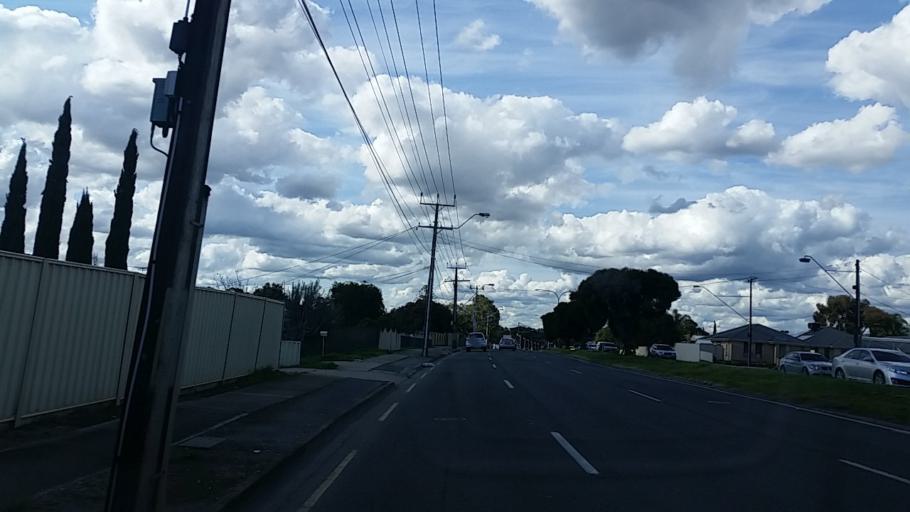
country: AU
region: South Australia
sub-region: Tea Tree Gully
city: Modbury
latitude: -34.8427
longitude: 138.6725
